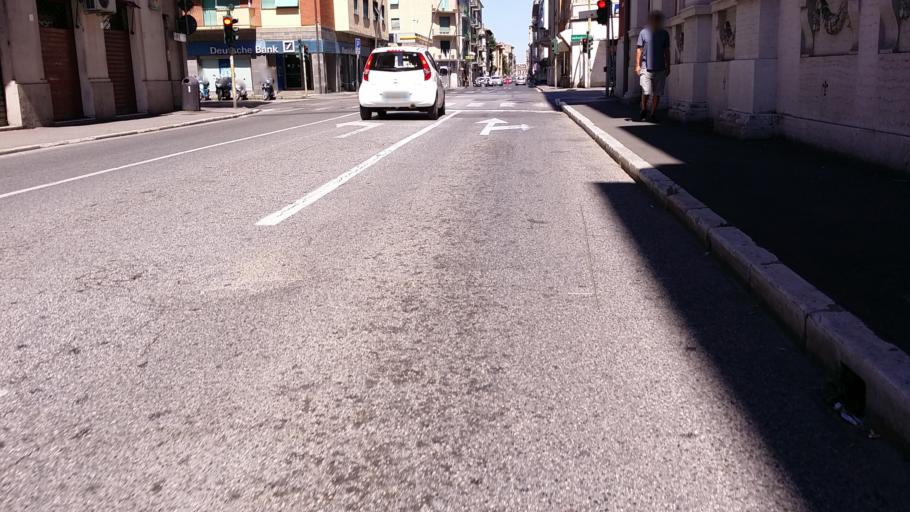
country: IT
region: Tuscany
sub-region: Provincia di Livorno
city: Livorno
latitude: 43.5388
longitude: 10.3173
